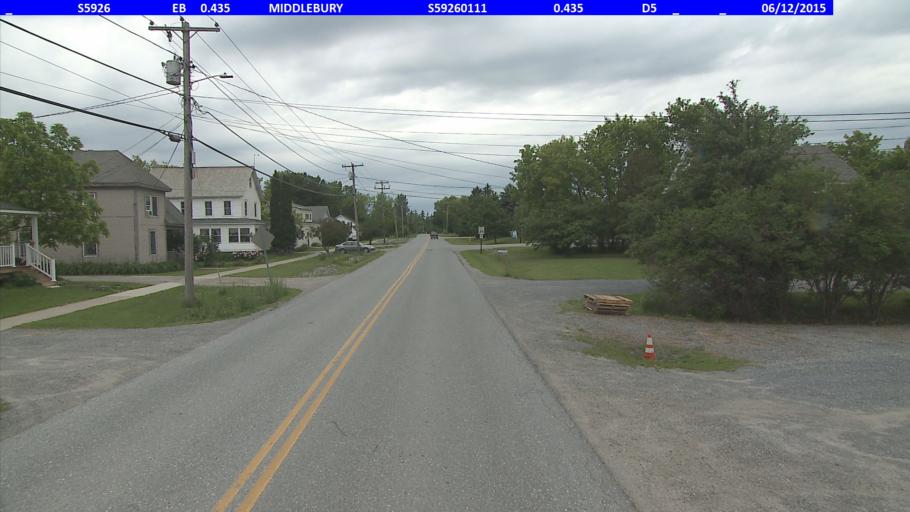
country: US
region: Vermont
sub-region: Addison County
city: Middlebury (village)
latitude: 44.0189
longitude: -73.1711
